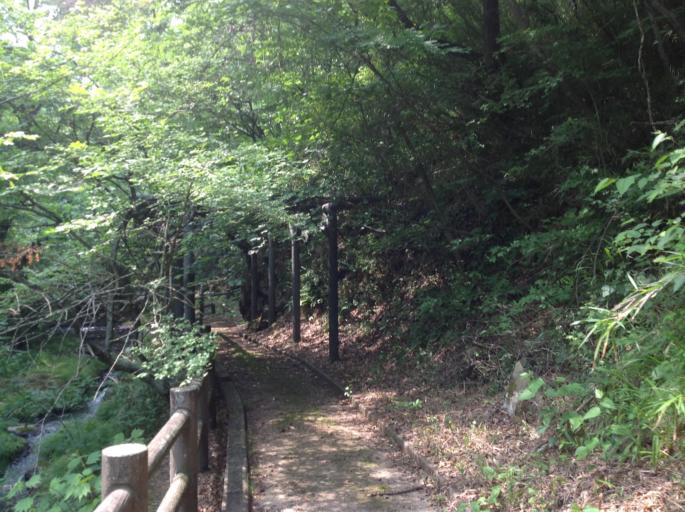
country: JP
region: Iwate
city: Ichinoseki
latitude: 38.8545
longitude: 141.2325
